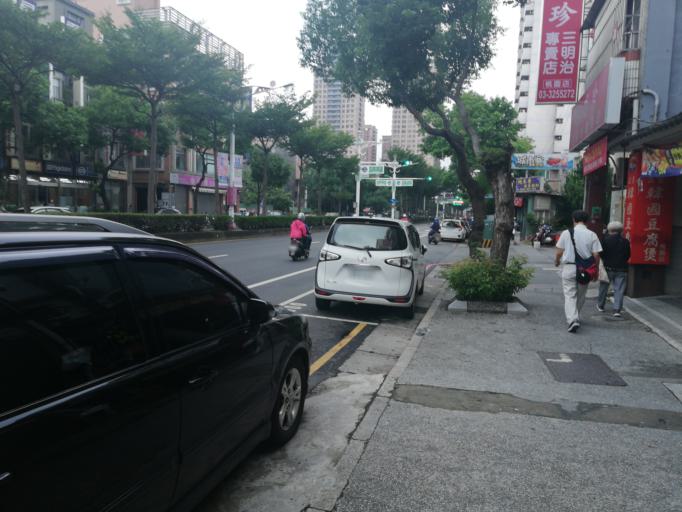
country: TW
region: Taiwan
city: Taoyuan City
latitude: 25.0081
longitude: 121.3027
